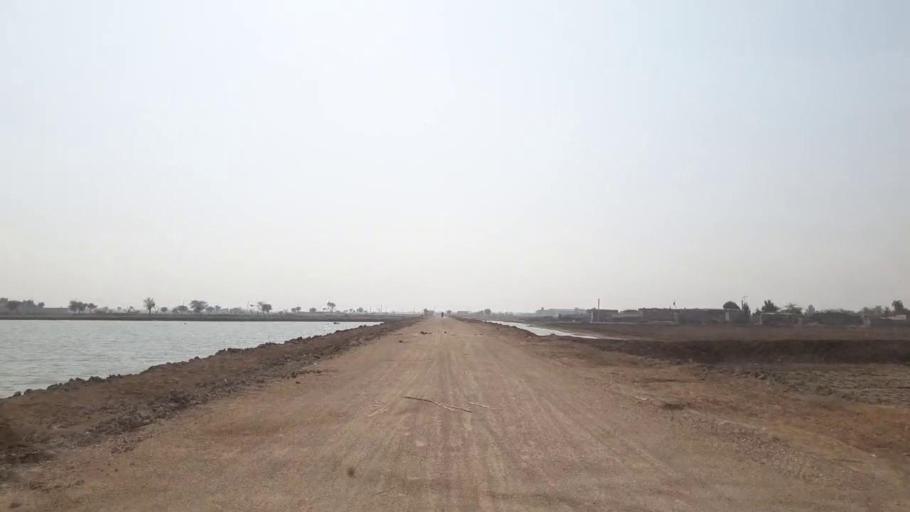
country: PK
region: Sindh
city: Mirpur Khas
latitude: 25.5586
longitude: 69.0470
